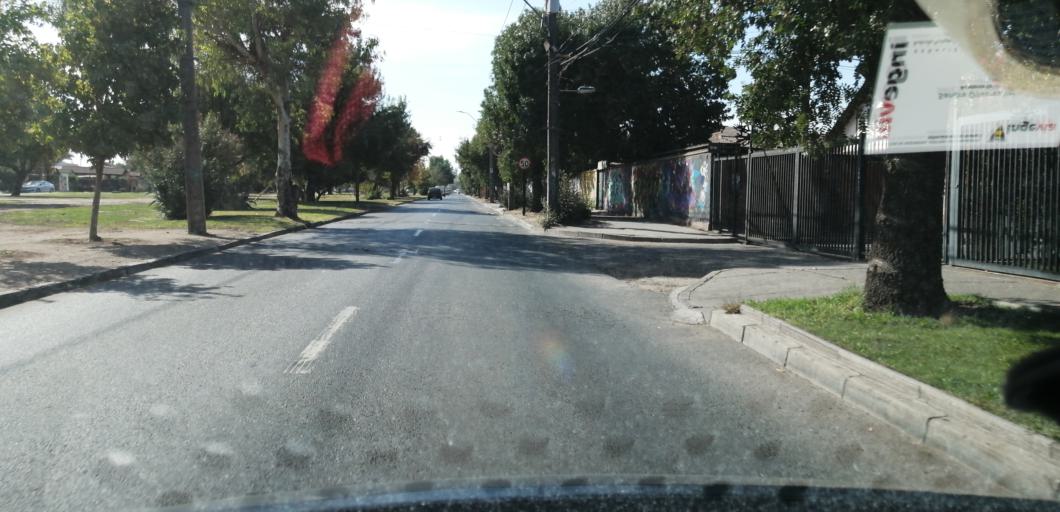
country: CL
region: Santiago Metropolitan
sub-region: Provincia de Santiago
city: Lo Prado
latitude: -33.4650
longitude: -70.7309
